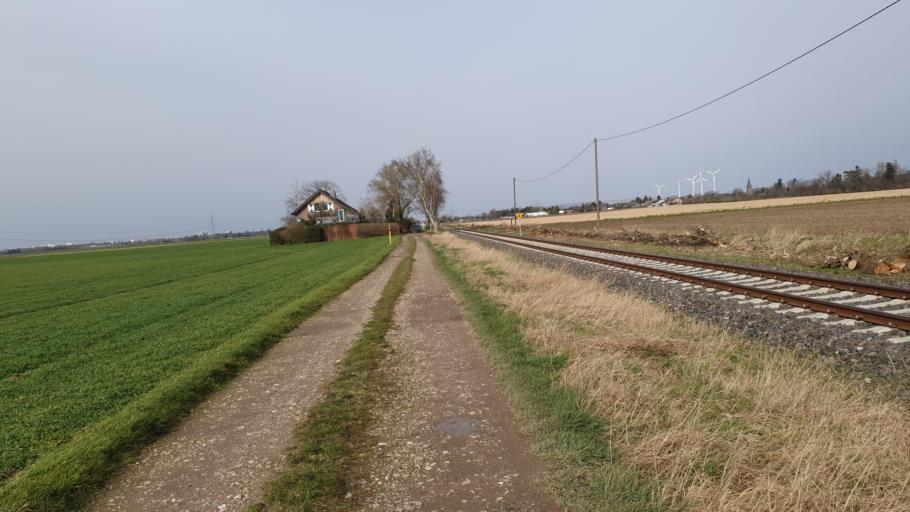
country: DE
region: North Rhine-Westphalia
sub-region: Regierungsbezirk Koln
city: Merzenich
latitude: 50.7851
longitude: 6.5444
